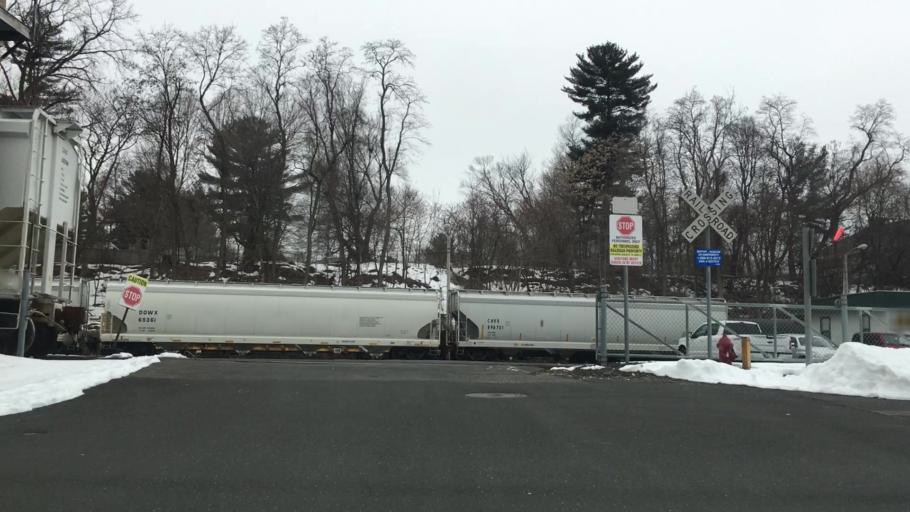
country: US
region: Massachusetts
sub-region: Hampden County
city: Westfield
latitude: 42.1317
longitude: -72.7448
